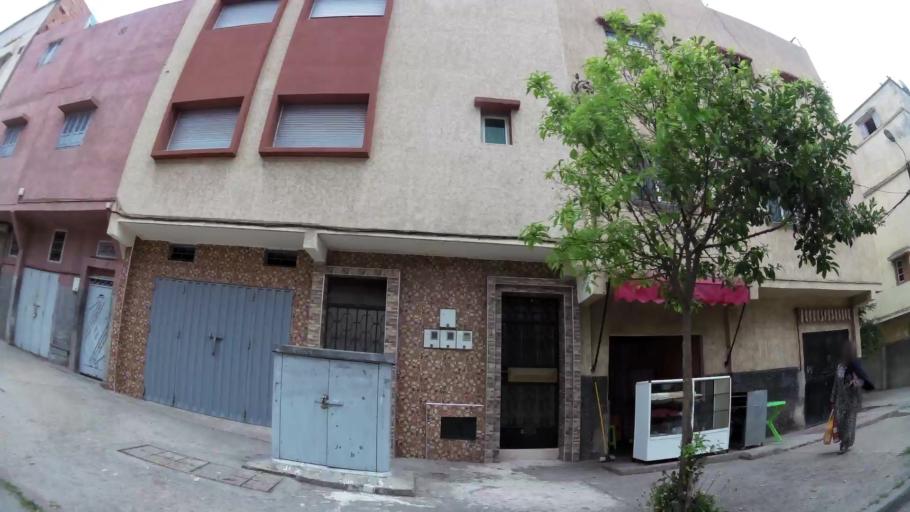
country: MA
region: Rabat-Sale-Zemmour-Zaer
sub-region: Rabat
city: Rabat
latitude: 34.0019
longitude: -6.8655
